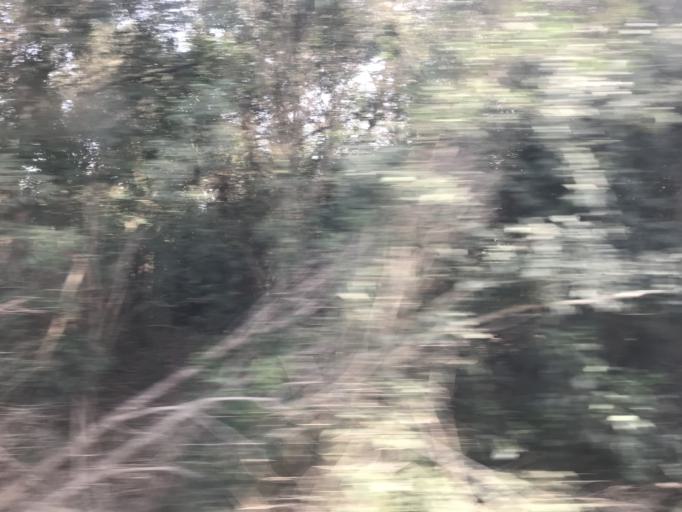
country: AR
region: Cordoba
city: Laguna Larga
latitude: -31.8012
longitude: -63.7819
